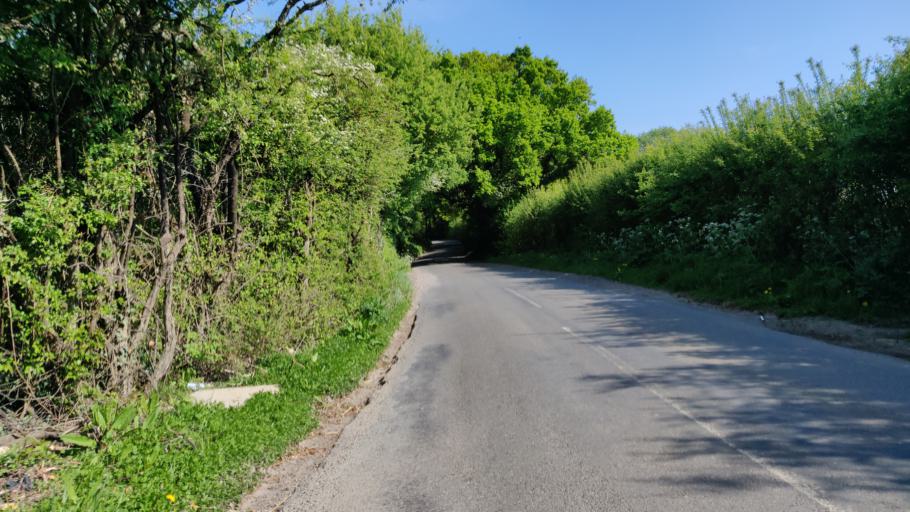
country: GB
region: England
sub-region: West Sussex
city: Billingshurst
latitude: 51.0271
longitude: -0.4162
